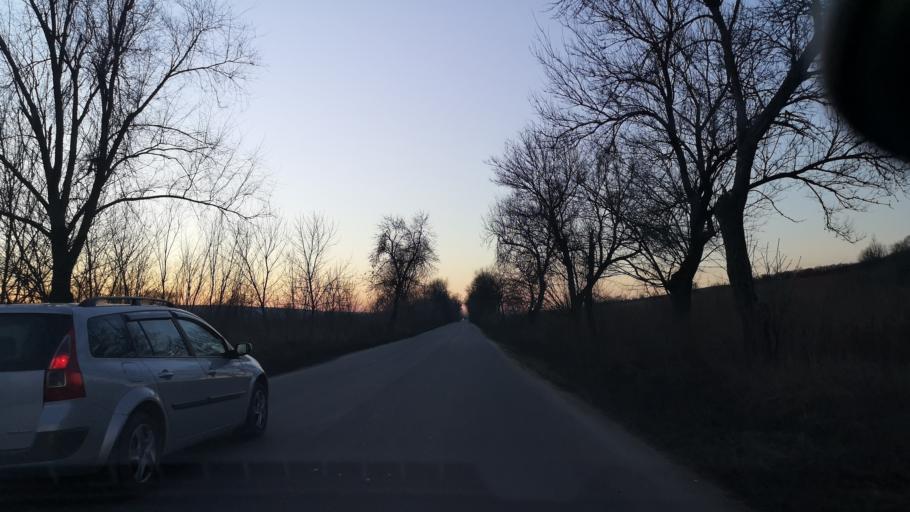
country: MD
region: Anenii Noi
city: Anenii Noi
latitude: 46.8881
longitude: 29.2639
